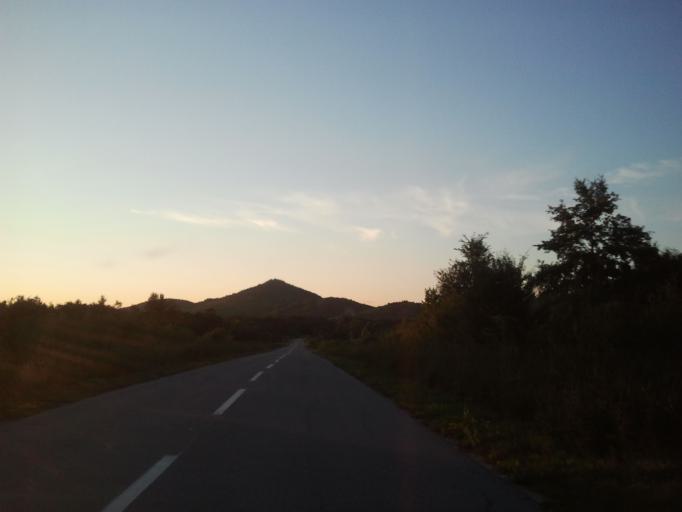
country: HR
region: Zadarska
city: Obrovac
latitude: 44.4164
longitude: 15.6638
